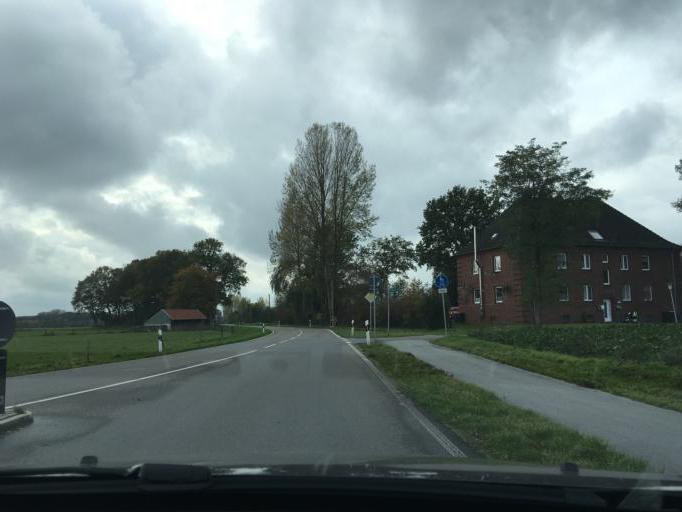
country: DE
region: North Rhine-Westphalia
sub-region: Regierungsbezirk Munster
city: Vreden
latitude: 52.0768
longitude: 6.7583
